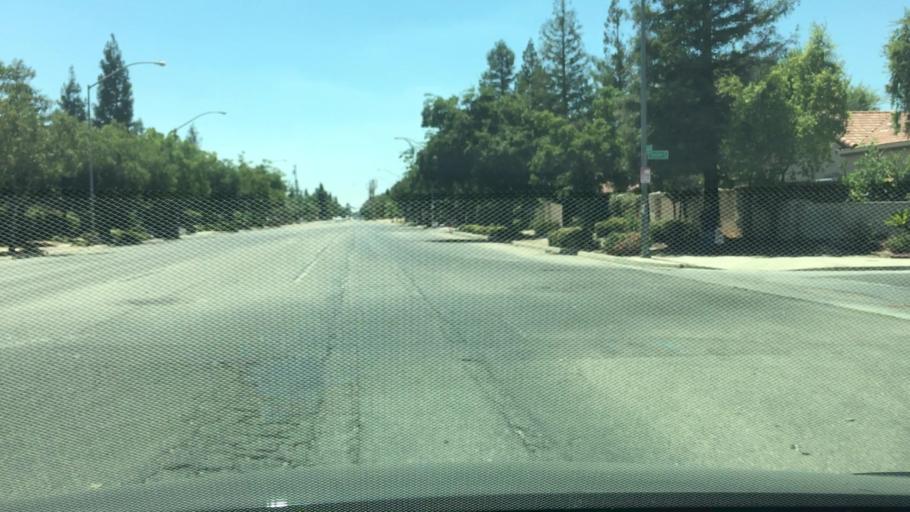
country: US
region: California
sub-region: Fresno County
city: Clovis
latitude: 36.8643
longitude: -119.7478
